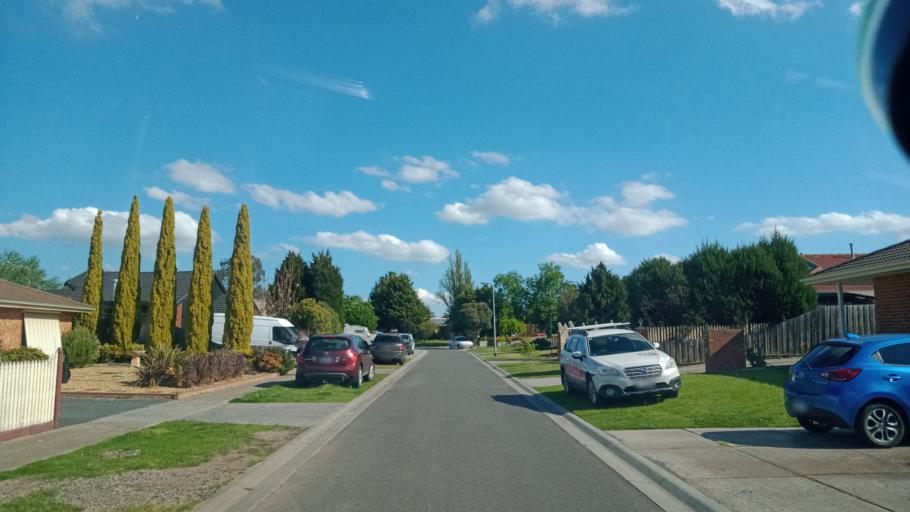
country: AU
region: Victoria
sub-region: Casey
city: Cranbourne West
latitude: -38.0968
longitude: 145.2666
